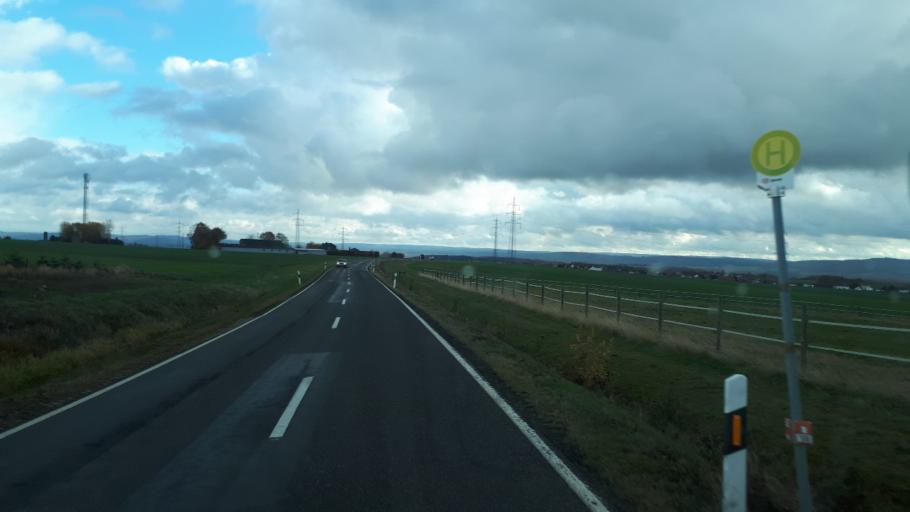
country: DE
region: Rheinland-Pfalz
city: Dunfus
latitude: 50.2140
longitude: 7.2331
